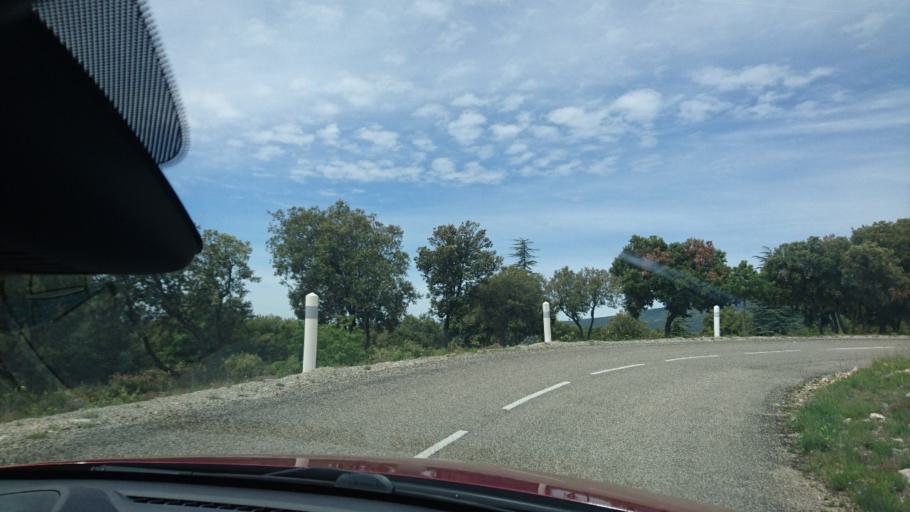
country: FR
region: Provence-Alpes-Cote d'Azur
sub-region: Departement du Vaucluse
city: Villes-sur-Auzon
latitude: 44.1051
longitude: 5.2558
